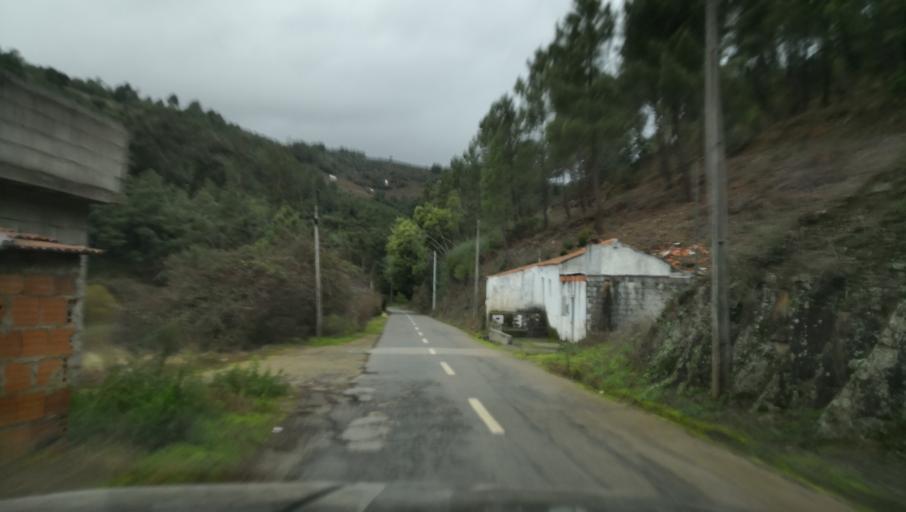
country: PT
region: Vila Real
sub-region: Vila Real
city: Vila Real
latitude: 41.2409
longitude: -7.7349
